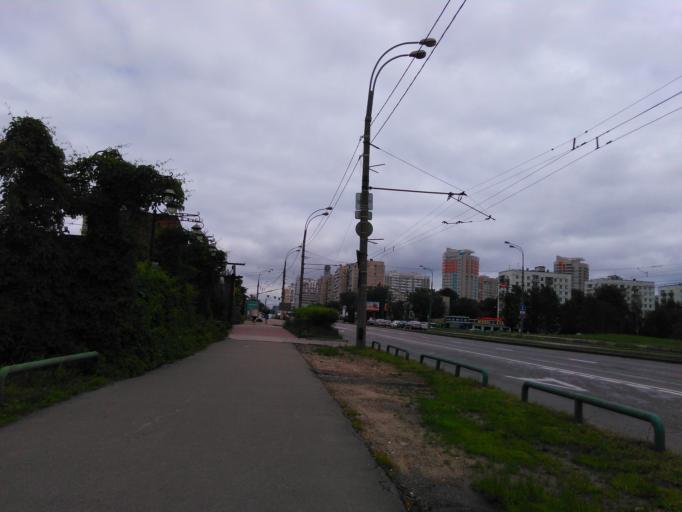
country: RU
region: Moscow
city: Troparevo
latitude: 55.6698
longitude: 37.4934
